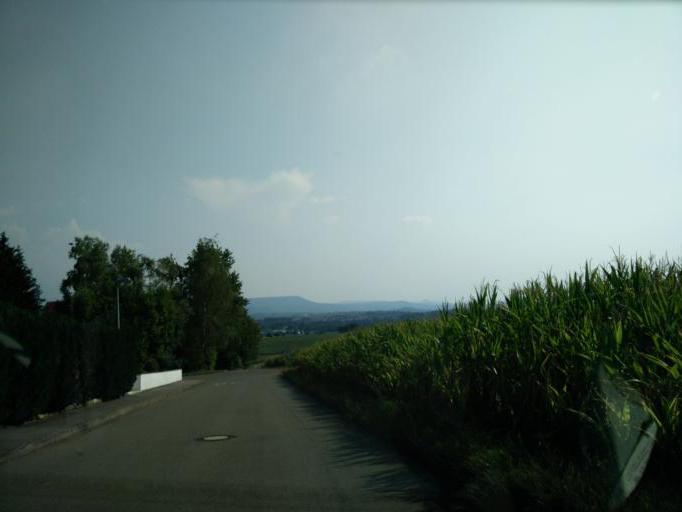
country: DE
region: Baden-Wuerttemberg
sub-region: Tuebingen Region
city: Gomaringen
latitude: 48.4721
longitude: 9.0827
